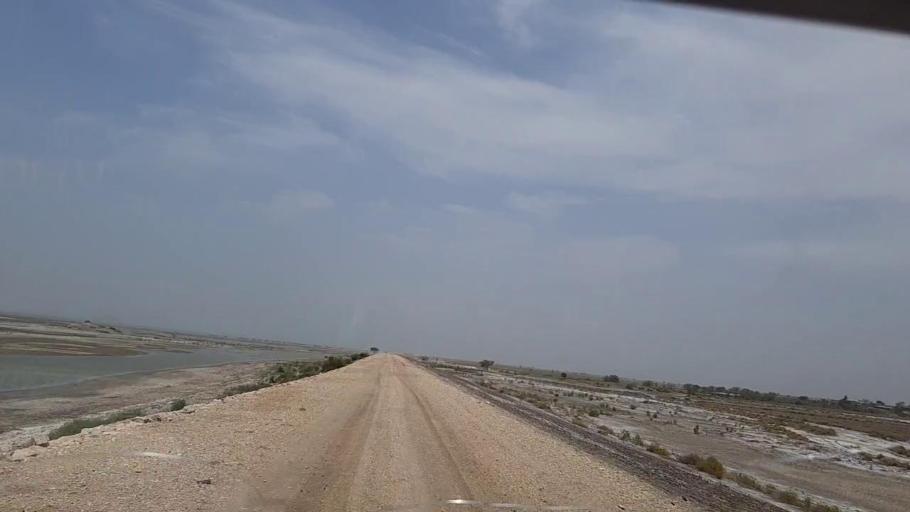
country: PK
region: Sindh
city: Sehwan
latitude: 26.4154
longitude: 67.7597
